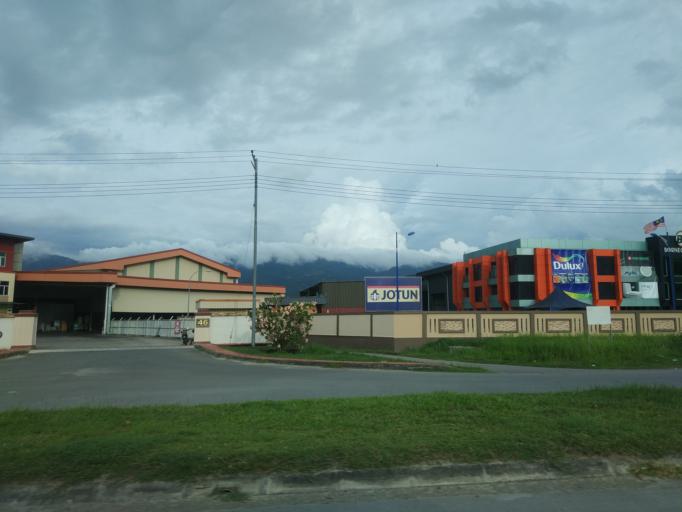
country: MY
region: Sabah
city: Kota Kinabalu
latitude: 6.0338
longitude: 116.1480
